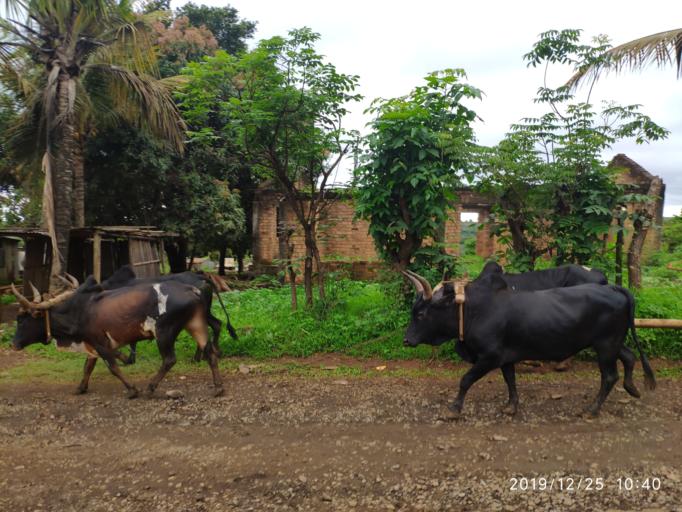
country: MG
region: Diana
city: Sadjoavato
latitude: -12.7529
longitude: 49.2368
